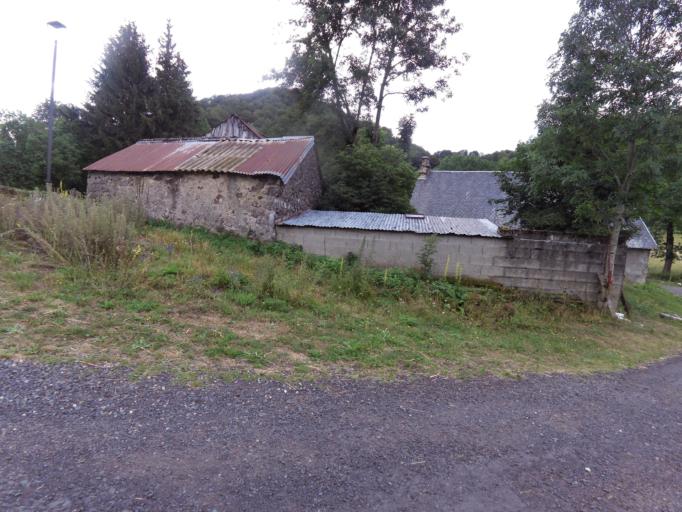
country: FR
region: Auvergne
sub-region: Departement du Puy-de-Dome
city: Mont-Dore
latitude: 45.4409
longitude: 2.9278
